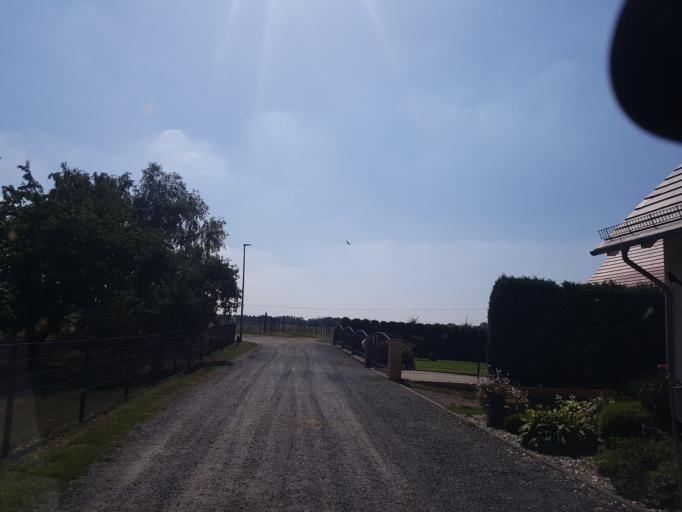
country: DE
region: Brandenburg
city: Hohenleipisch
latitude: 51.4841
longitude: 13.5355
